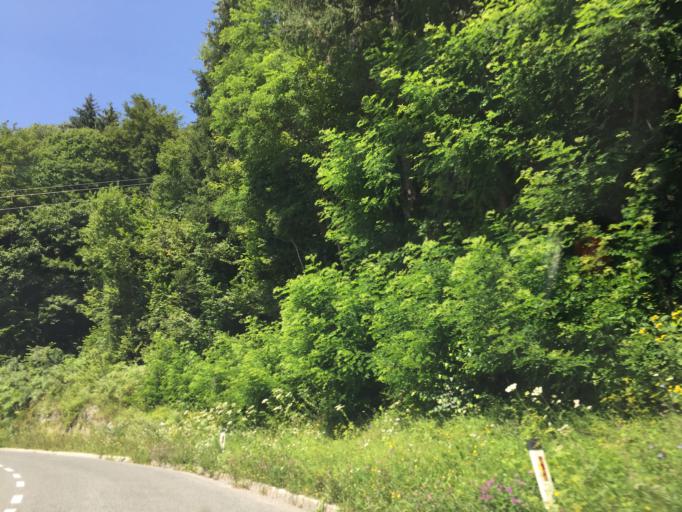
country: SI
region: Trbovlje
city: Trbovlje
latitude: 46.1857
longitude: 15.0605
